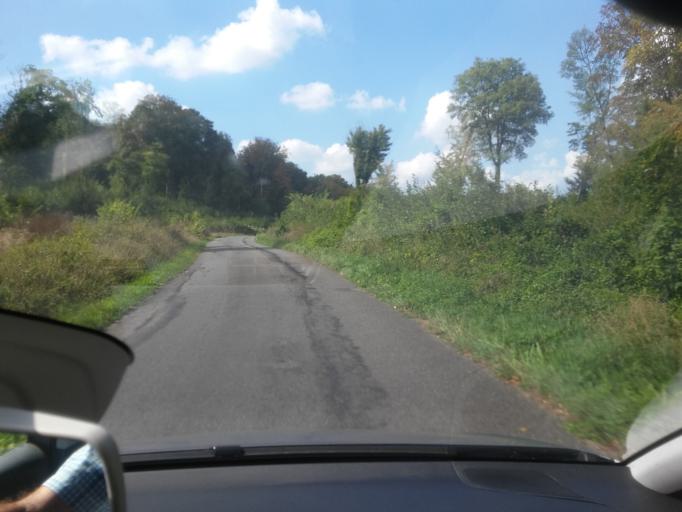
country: FR
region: Lorraine
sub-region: Departement de la Meuse
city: Montmedy
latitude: 49.4966
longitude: 5.3975
